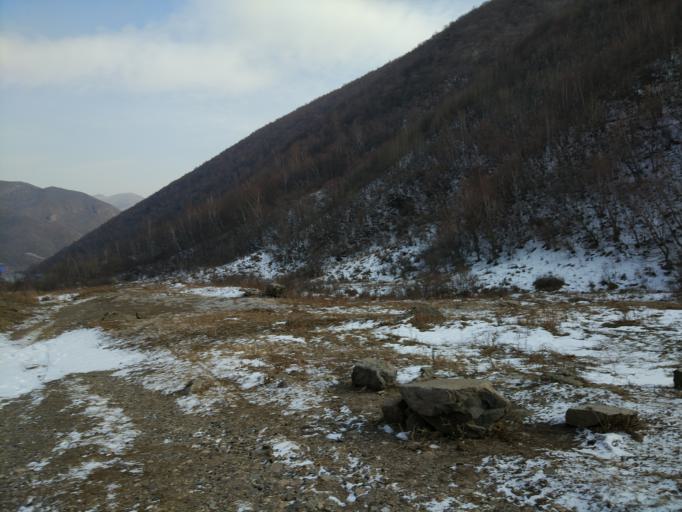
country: CN
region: Hebei
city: Xiwanzi
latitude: 40.8432
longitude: 115.4612
